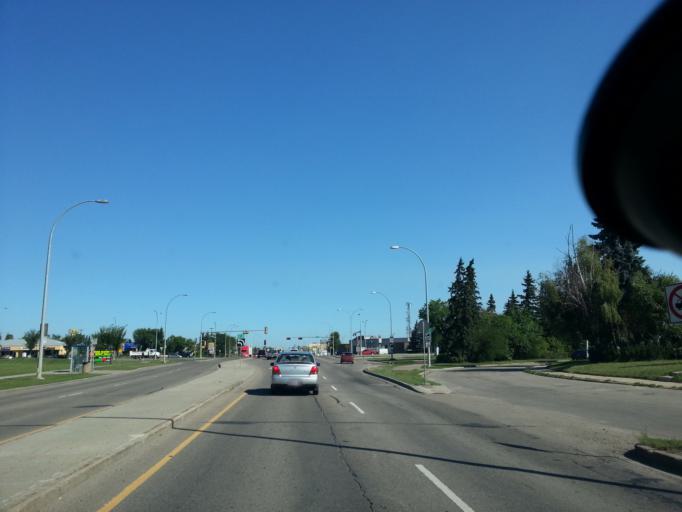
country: CA
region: Alberta
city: Edmonton
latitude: 53.5980
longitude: -113.5412
